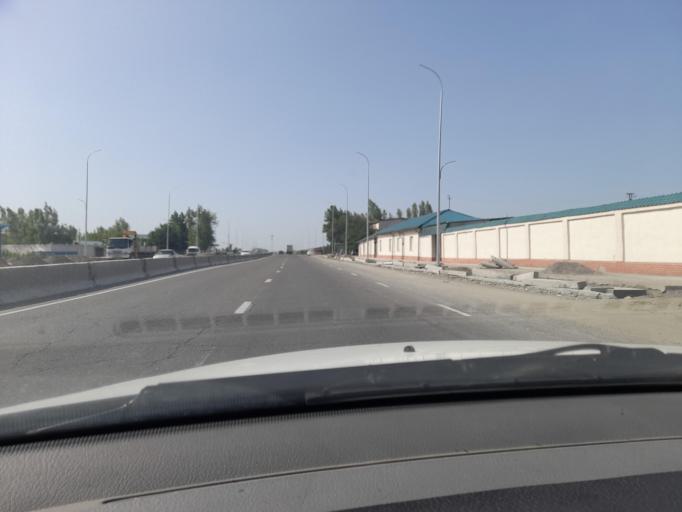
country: UZ
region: Samarqand
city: Daxbet
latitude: 39.7433
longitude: 66.9255
